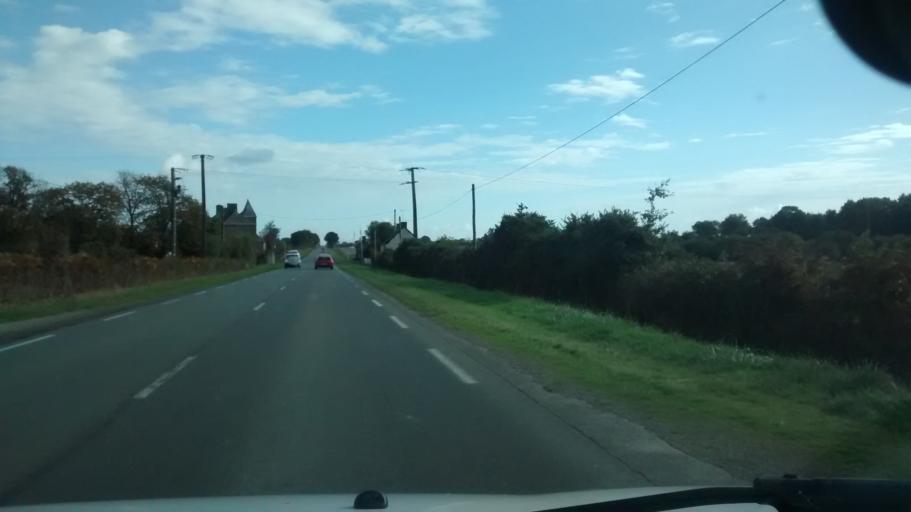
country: FR
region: Pays de la Loire
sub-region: Departement de Maine-et-Loire
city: Pouance
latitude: 47.7444
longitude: -1.2305
